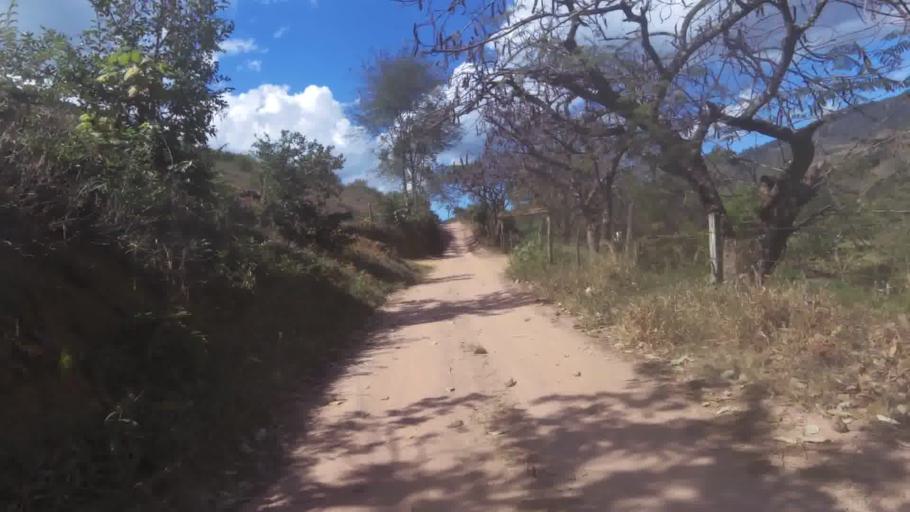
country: BR
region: Espirito Santo
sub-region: Vargem Alta
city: Vargem Alta
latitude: -20.6602
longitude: -41.0547
